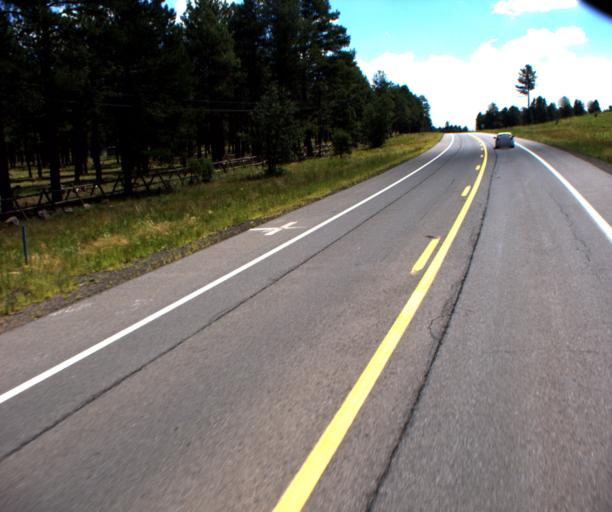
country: US
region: Arizona
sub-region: Coconino County
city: Flagstaff
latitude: 35.1893
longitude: -111.6953
